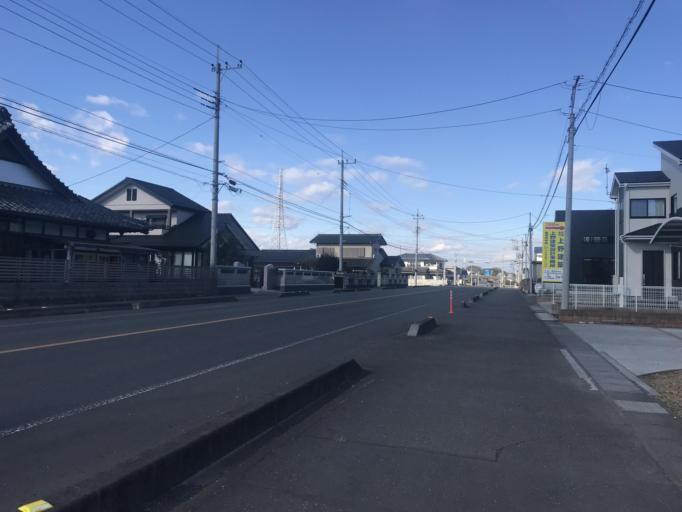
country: JP
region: Tochigi
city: Kaminokawa
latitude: 36.3851
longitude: 139.8754
